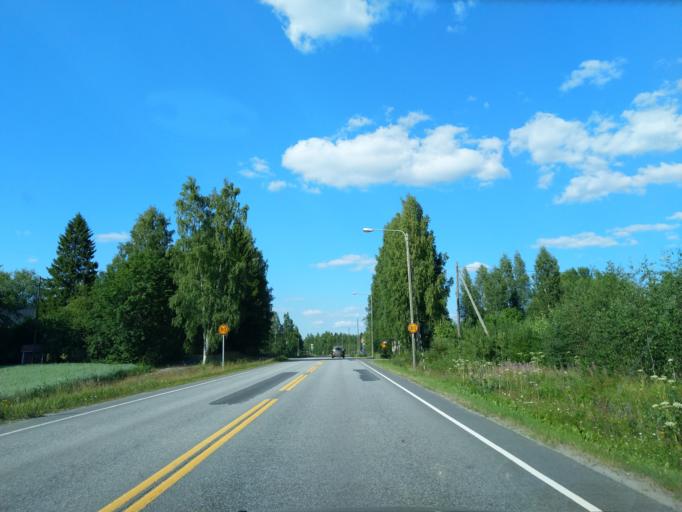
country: FI
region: Pirkanmaa
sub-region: Luoteis-Pirkanmaa
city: Kihnioe
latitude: 62.1737
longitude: 23.1671
